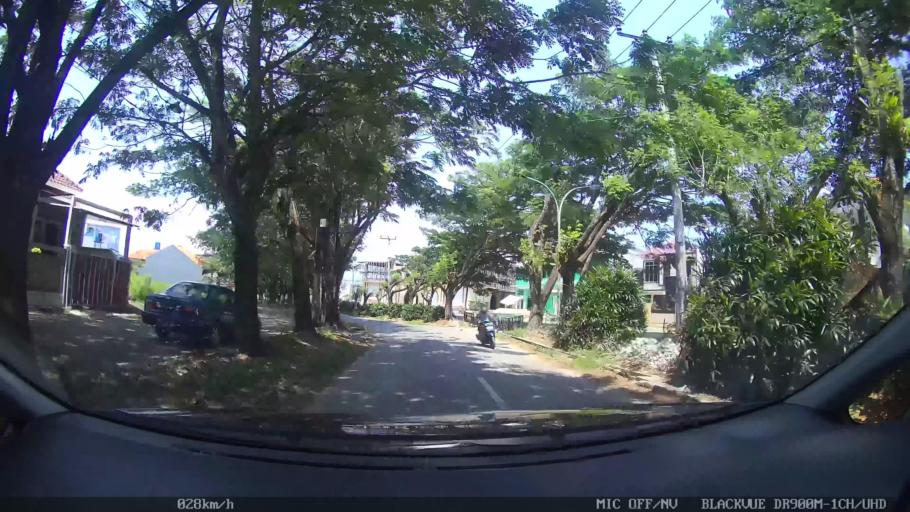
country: ID
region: Lampung
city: Kedaton
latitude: -5.3612
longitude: 105.2707
